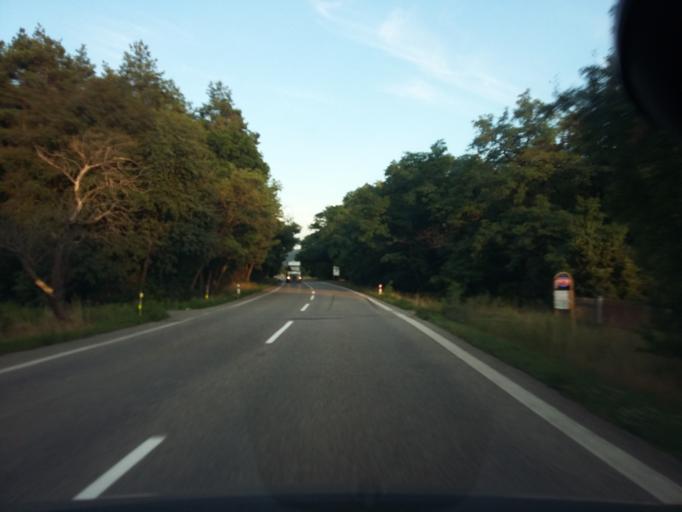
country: SK
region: Bratislavsky
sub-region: Okres Malacky
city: Malacky
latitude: 48.3883
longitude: 17.1003
